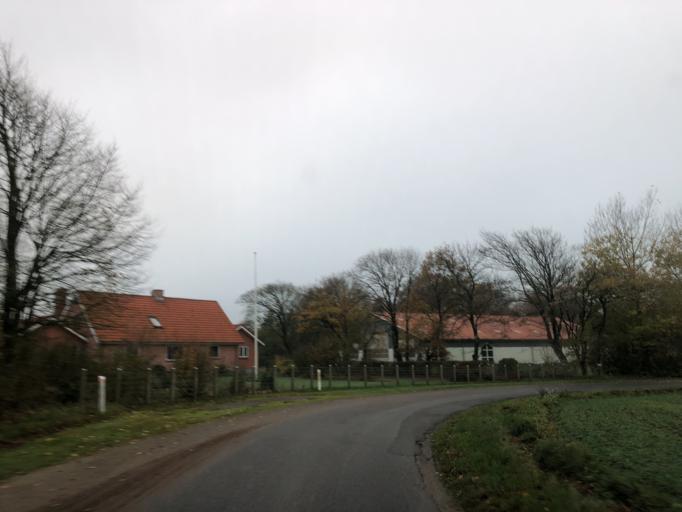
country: DK
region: Central Jutland
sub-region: Ringkobing-Skjern Kommune
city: Videbaek
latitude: 56.1961
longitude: 8.6530
